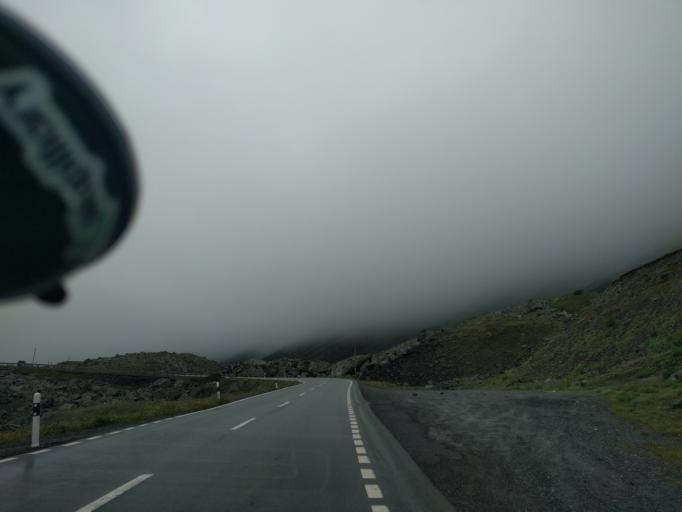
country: CH
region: Grisons
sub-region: Praettigau/Davos District
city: Davos
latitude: 46.7549
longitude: 9.9411
